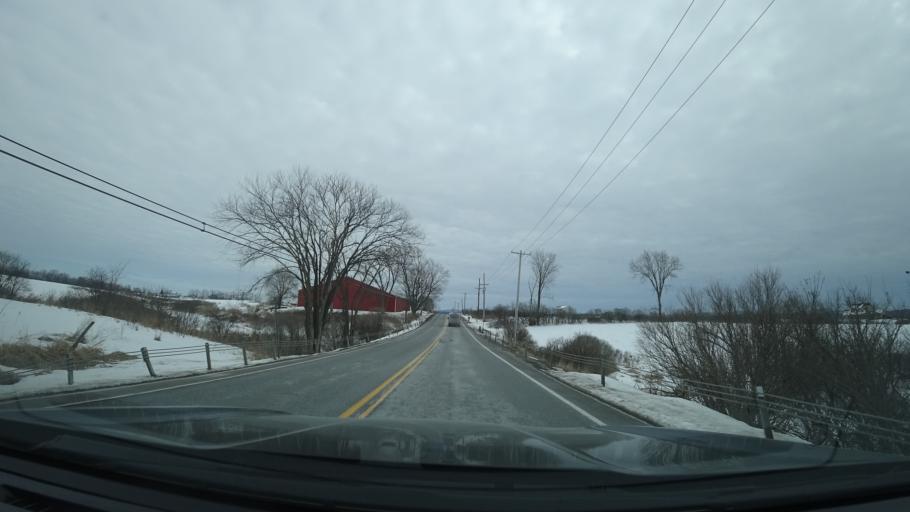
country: US
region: New York
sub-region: Washington County
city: Fort Edward
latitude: 43.2640
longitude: -73.5489
